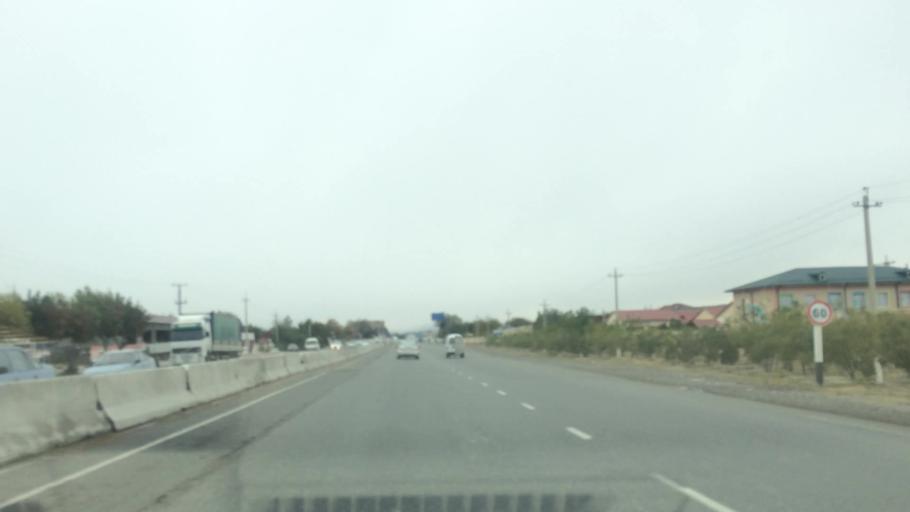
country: UZ
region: Samarqand
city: Jomboy
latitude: 39.7013
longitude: 67.0770
